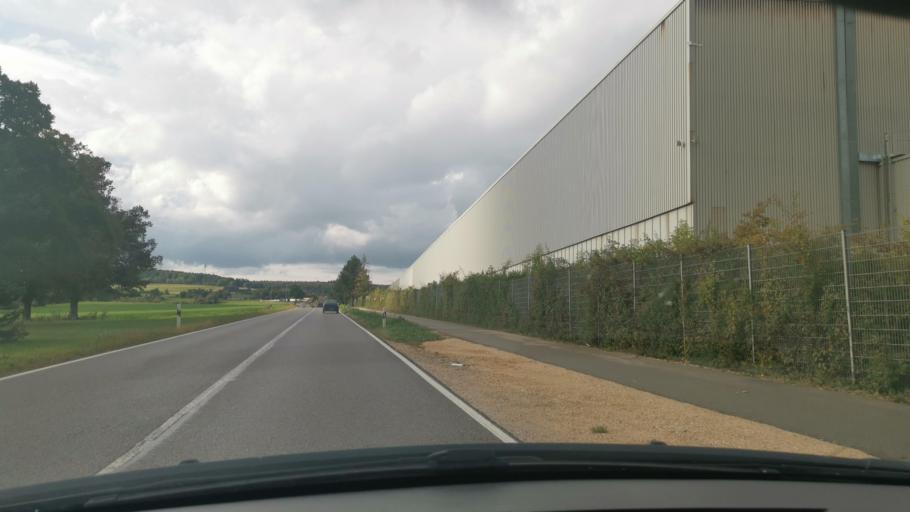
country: DE
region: Baden-Wuerttemberg
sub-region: Tuebingen Region
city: Ehingen
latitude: 48.2938
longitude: 9.7084
